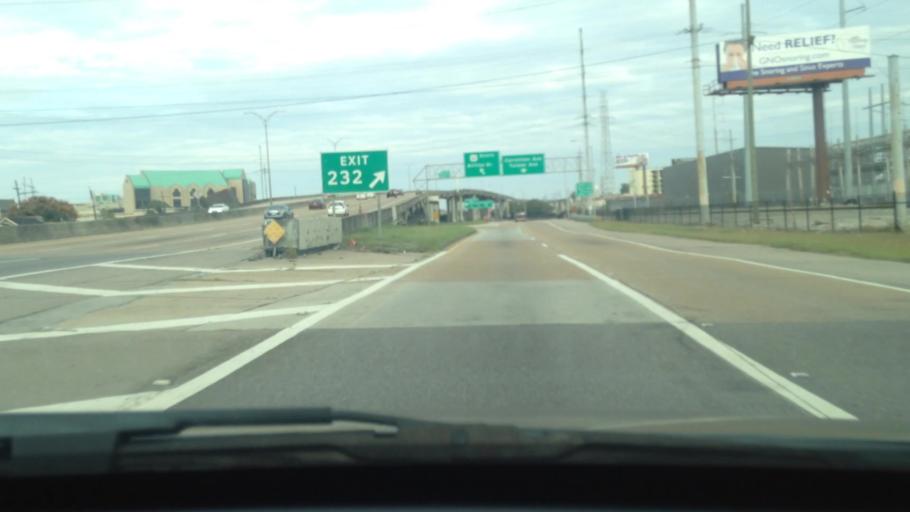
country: US
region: Louisiana
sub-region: Orleans Parish
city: New Orleans
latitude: 29.9637
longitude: -90.1021
